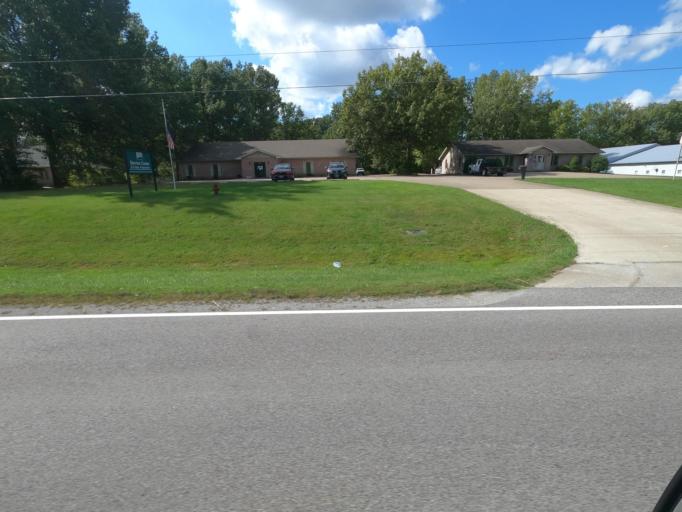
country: US
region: Illinois
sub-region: Johnson County
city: Vienna
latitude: 37.4256
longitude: -88.8930
